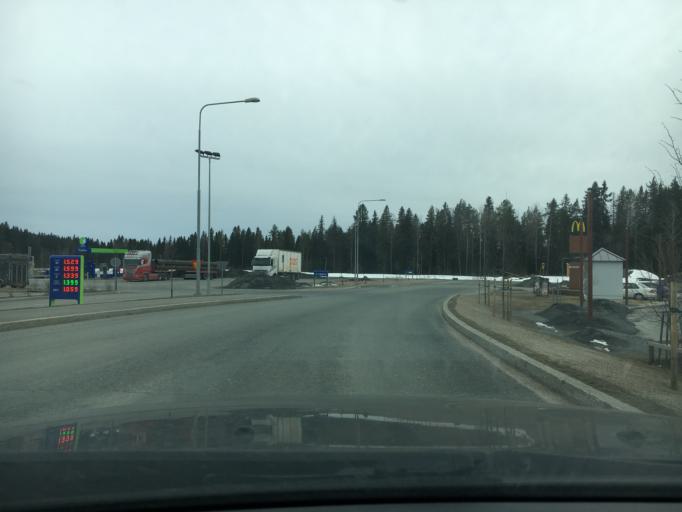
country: FI
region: Northern Savo
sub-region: Kuopio
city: Kuopio
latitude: 62.8209
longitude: 27.6073
